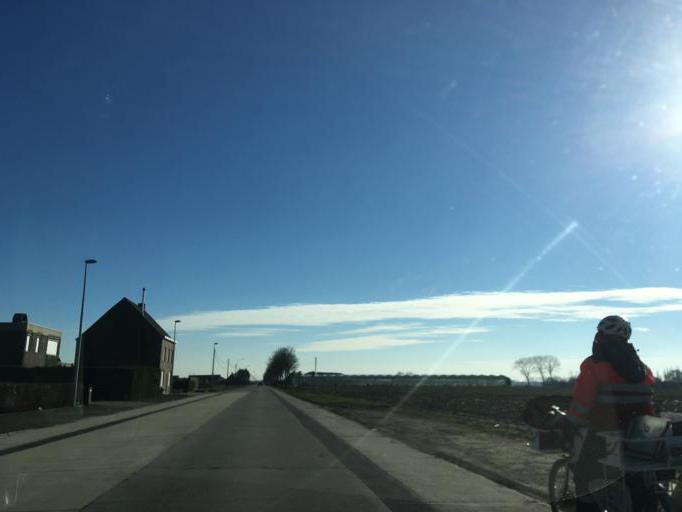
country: BE
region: Flanders
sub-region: Provincie West-Vlaanderen
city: Pittem
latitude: 51.0174
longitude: 3.2700
